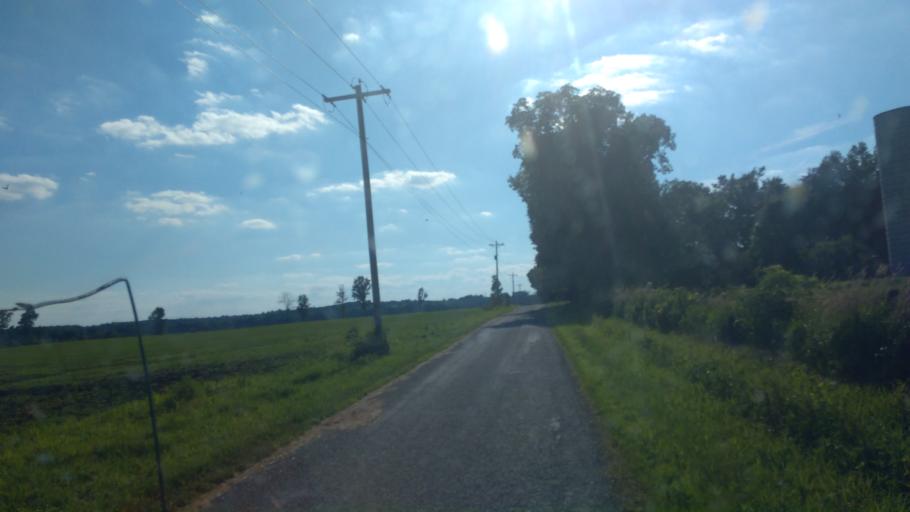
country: US
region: Ohio
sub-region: Wayne County
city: Shreve
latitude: 40.7341
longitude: -82.0772
